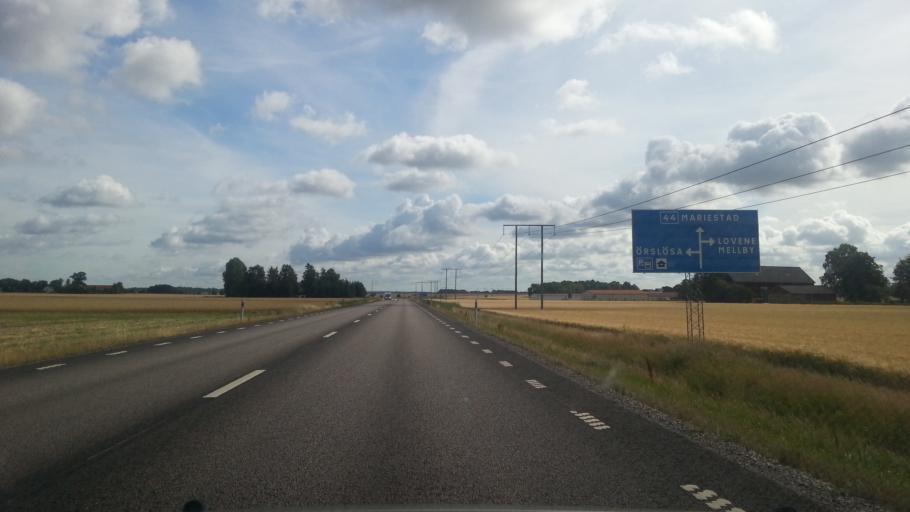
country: SE
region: Vaestra Goetaland
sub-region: Lidkopings Kommun
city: Lidkoping
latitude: 58.4622
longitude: 13.0328
